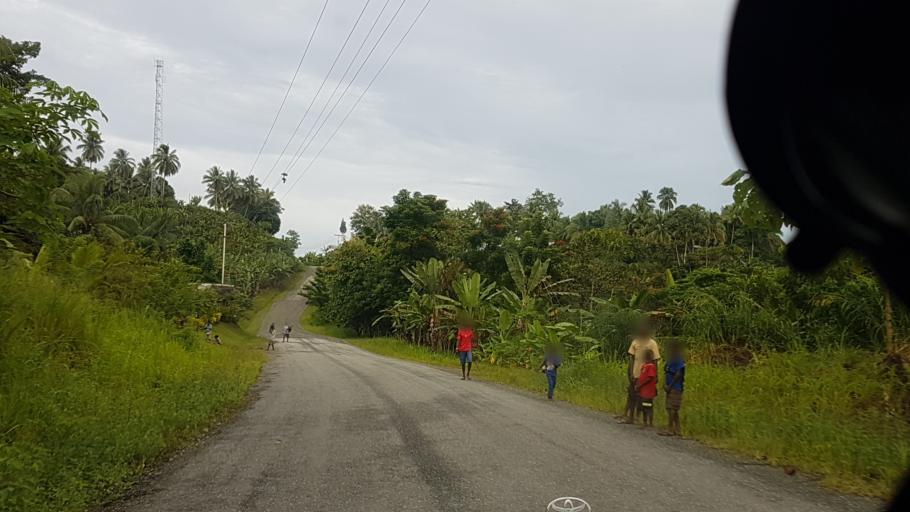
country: PG
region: East Sepik
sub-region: Wewak
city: Wewak
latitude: -3.6836
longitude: 143.2822
